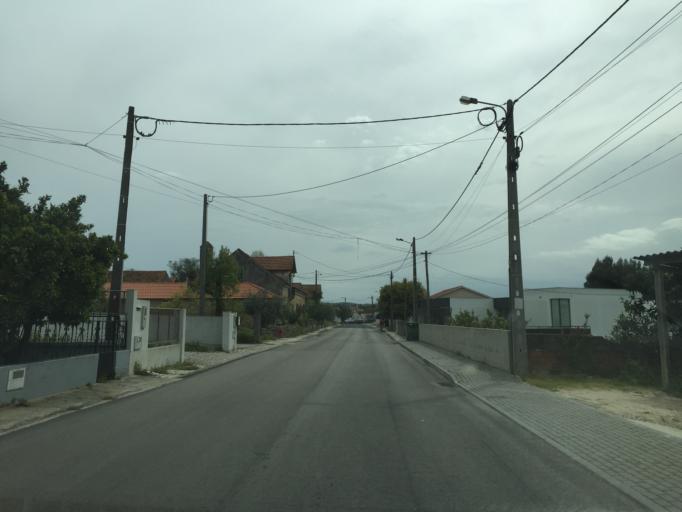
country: PT
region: Leiria
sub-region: Leiria
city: Caranguejeira
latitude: 39.7841
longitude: -8.7483
